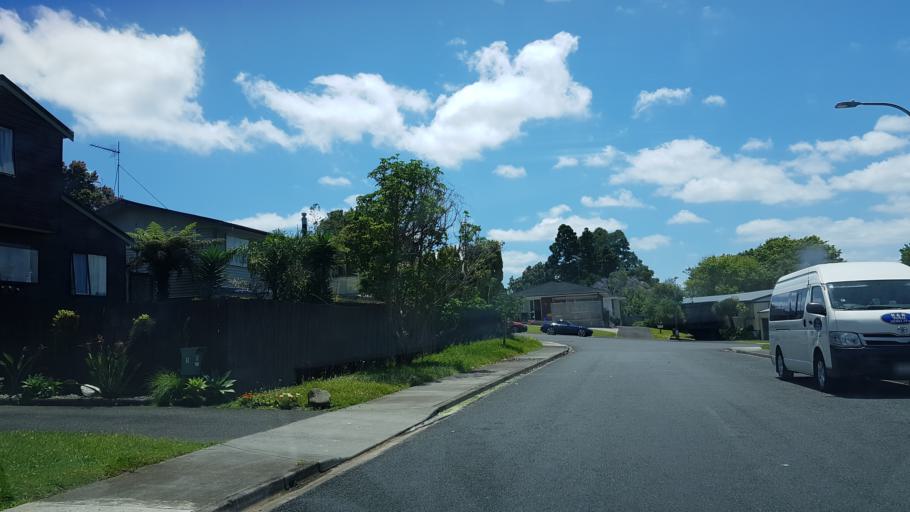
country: NZ
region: Auckland
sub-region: Auckland
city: North Shore
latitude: -36.7892
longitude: 174.7267
